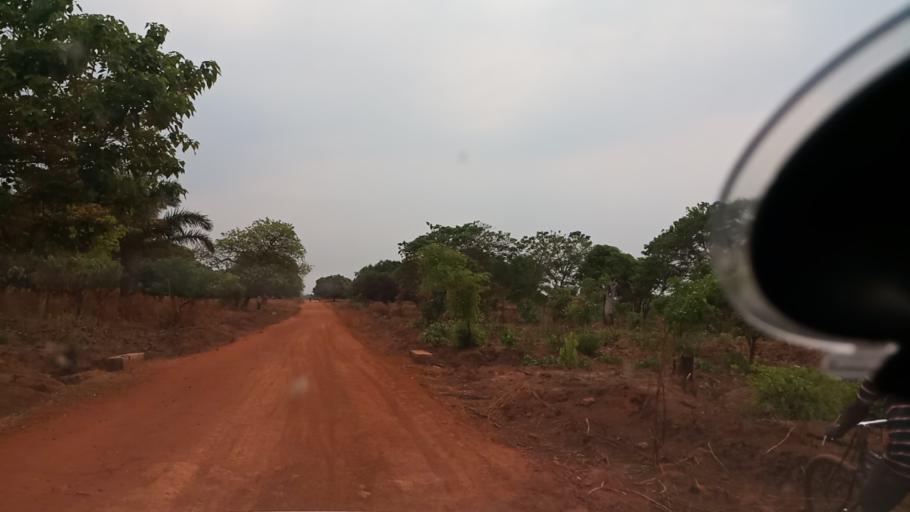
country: ZM
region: Luapula
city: Nchelenge
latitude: -9.0666
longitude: 28.3542
